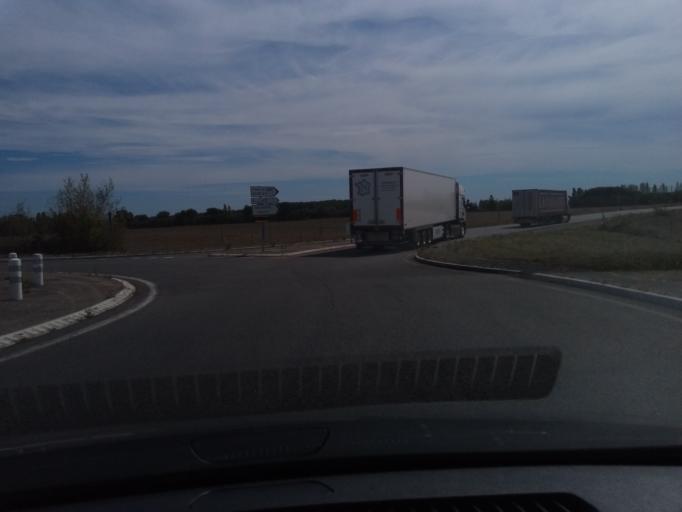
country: FR
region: Poitou-Charentes
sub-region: Departement de la Vienne
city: Terce
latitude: 46.4855
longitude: 0.5171
